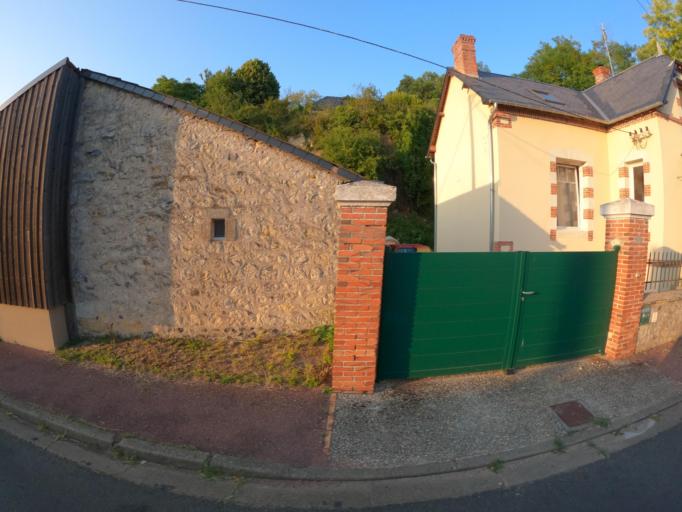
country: FR
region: Pays de la Loire
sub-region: Departement de la Sarthe
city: Parce-sur-Sarthe
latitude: 47.8630
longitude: -0.2003
